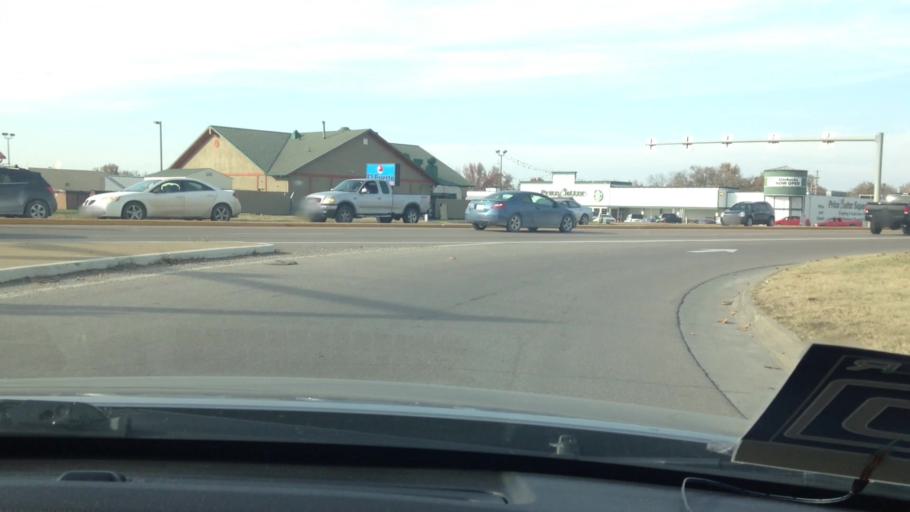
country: US
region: Missouri
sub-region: Henry County
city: Clinton
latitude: 38.3663
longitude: -93.7518
